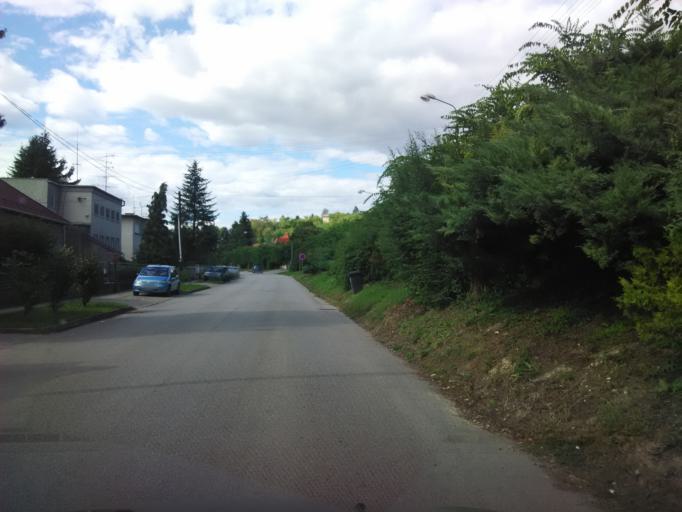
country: SK
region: Nitriansky
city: Levice
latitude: 48.2191
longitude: 18.6174
